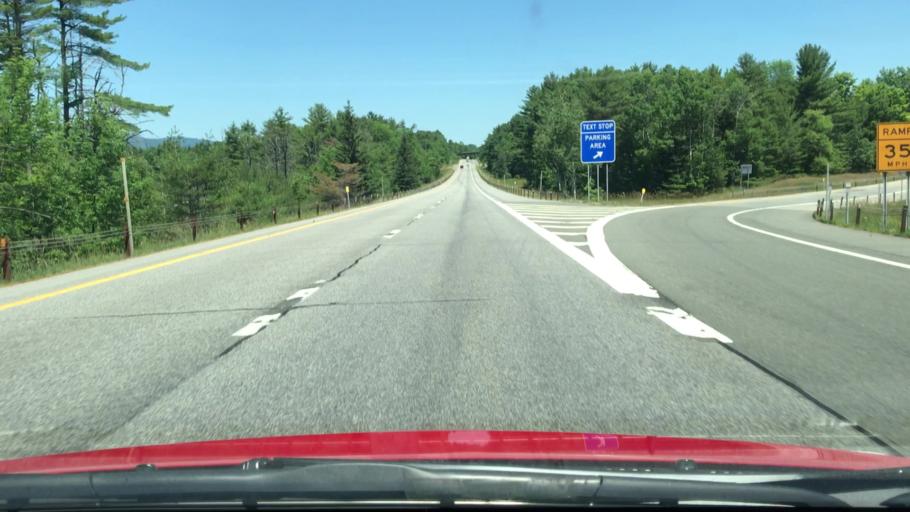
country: US
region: New York
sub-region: Essex County
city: Elizabethtown
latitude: 44.1590
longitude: -73.5831
